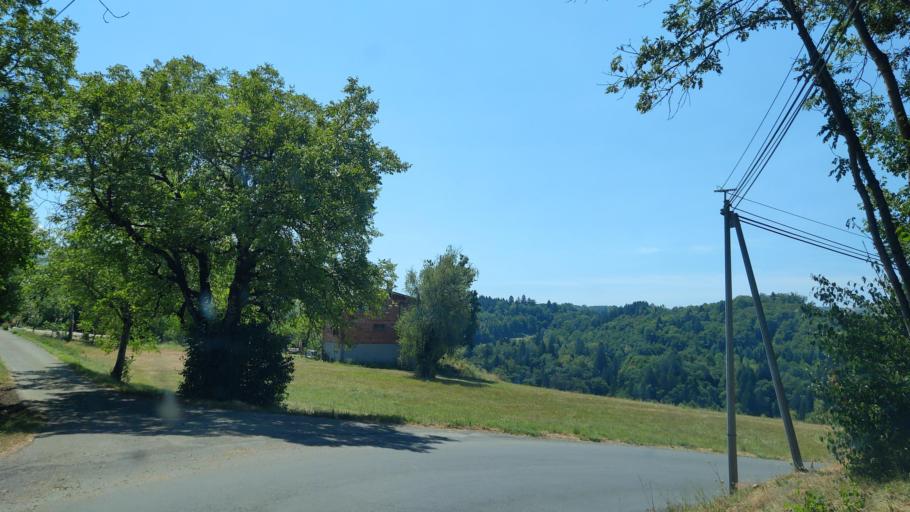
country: FR
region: Rhone-Alpes
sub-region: Departement de la Savoie
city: Novalaise
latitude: 45.5896
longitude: 5.7876
